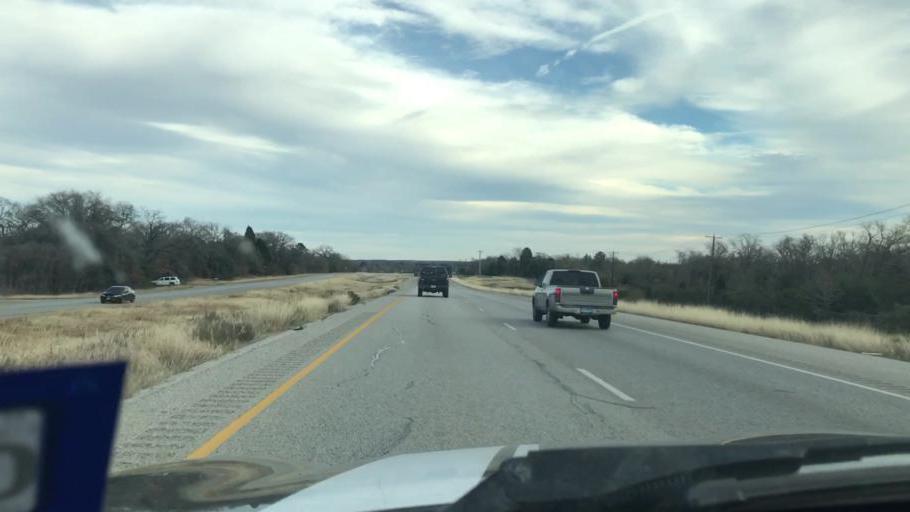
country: US
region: Texas
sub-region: Bastrop County
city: Elgin
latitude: 30.3243
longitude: -97.3264
